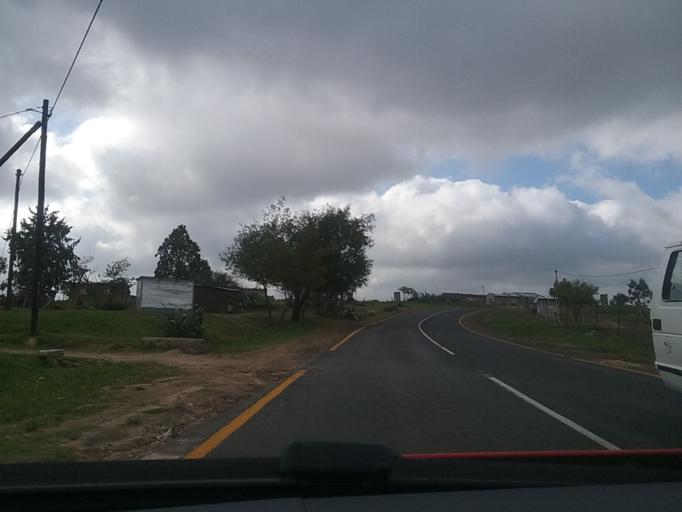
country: LS
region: Berea
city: Teyateyaneng
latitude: -29.1710
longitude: 27.7802
